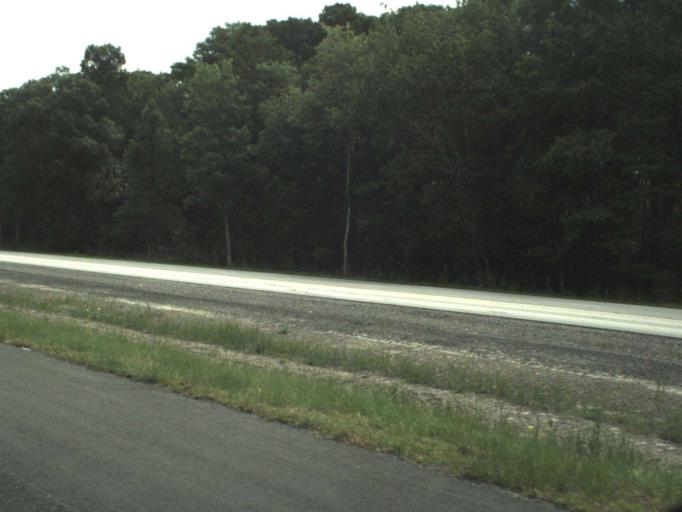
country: US
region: Florida
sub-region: Volusia County
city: Lake Helen
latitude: 29.0535
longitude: -81.1979
